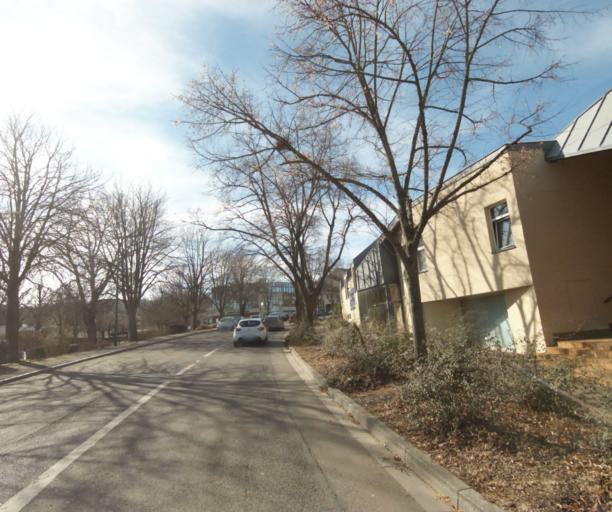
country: FR
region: Lorraine
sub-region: Departement de Meurthe-et-Moselle
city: Villers-les-Nancy
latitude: 48.6721
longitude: 6.1542
